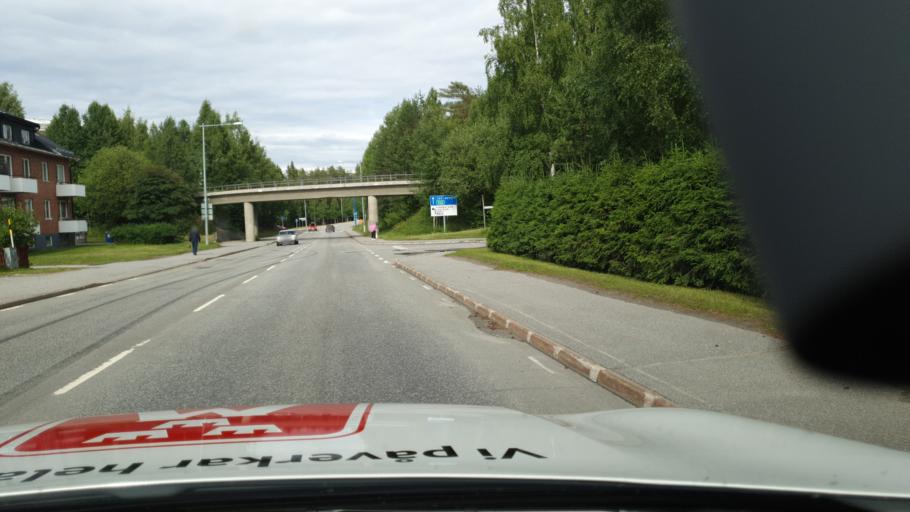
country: SE
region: Vaesterbotten
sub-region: Lycksele Kommun
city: Lycksele
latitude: 64.5899
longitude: 18.6695
